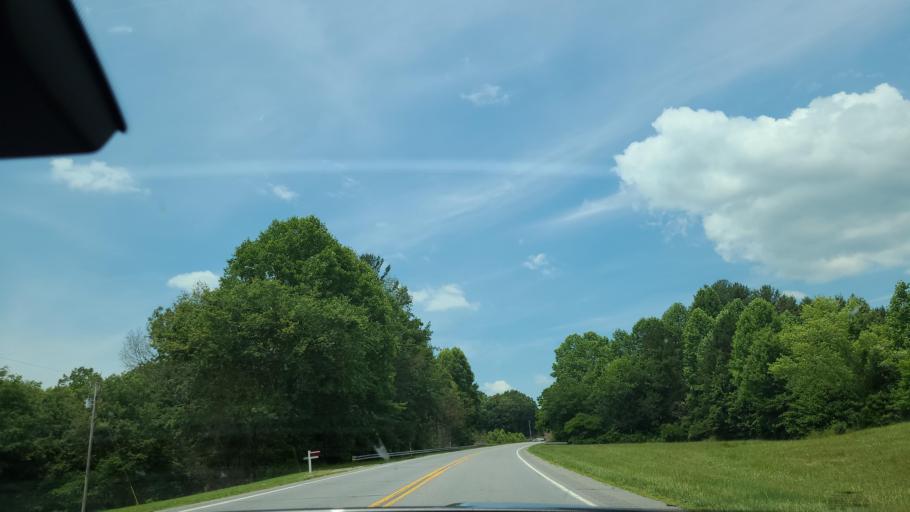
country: US
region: Georgia
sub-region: Towns County
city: Hiawassee
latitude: 35.0272
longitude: -83.7173
